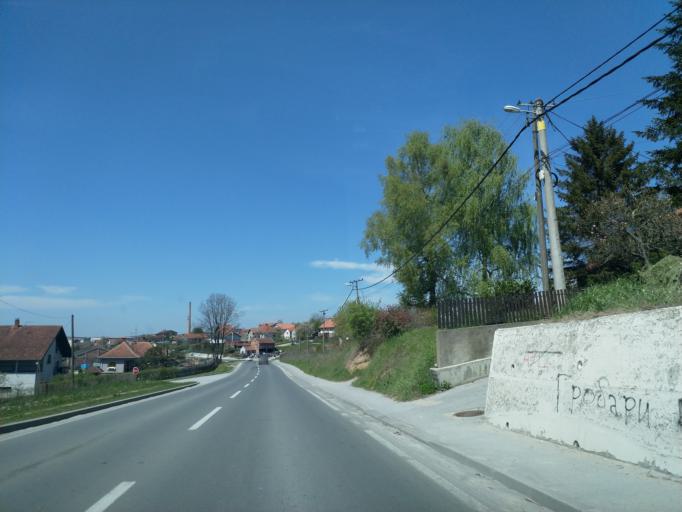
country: RS
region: Central Serbia
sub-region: Sumadijski Okrug
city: Arangelovac
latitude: 44.3229
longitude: 20.5356
